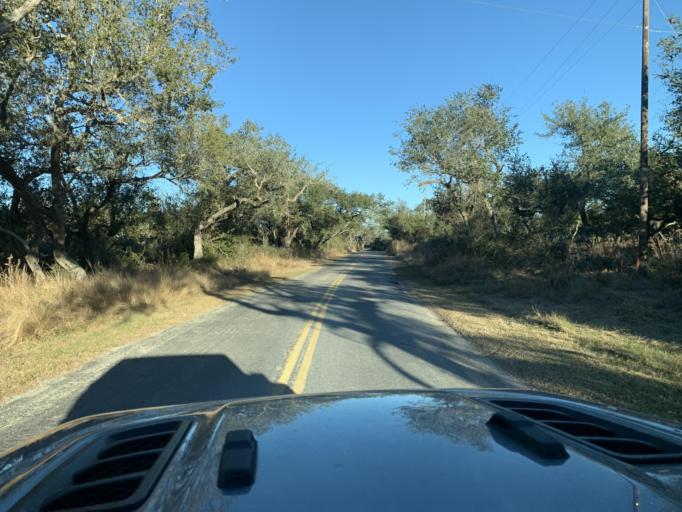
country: US
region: Texas
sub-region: Aransas County
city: Fulton
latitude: 28.1518
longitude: -96.9842
